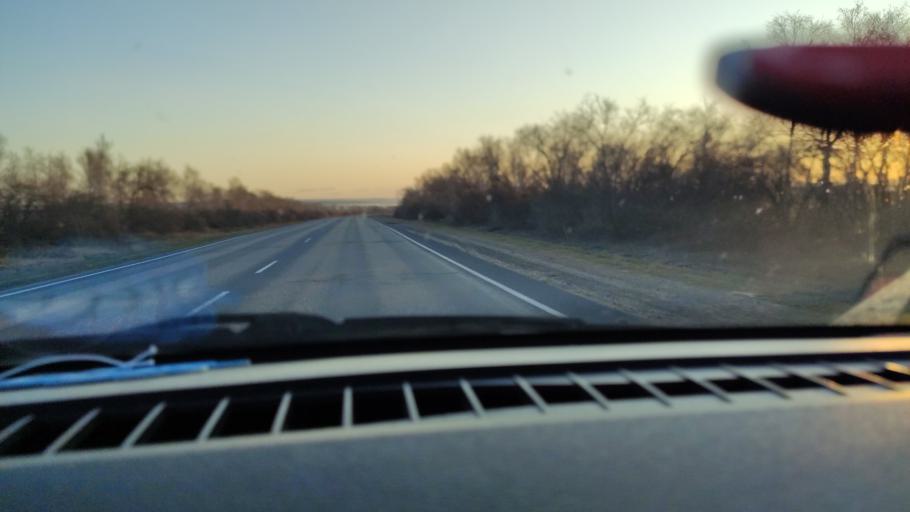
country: RU
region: Saratov
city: Sinodskoye
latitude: 51.9512
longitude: 46.6087
